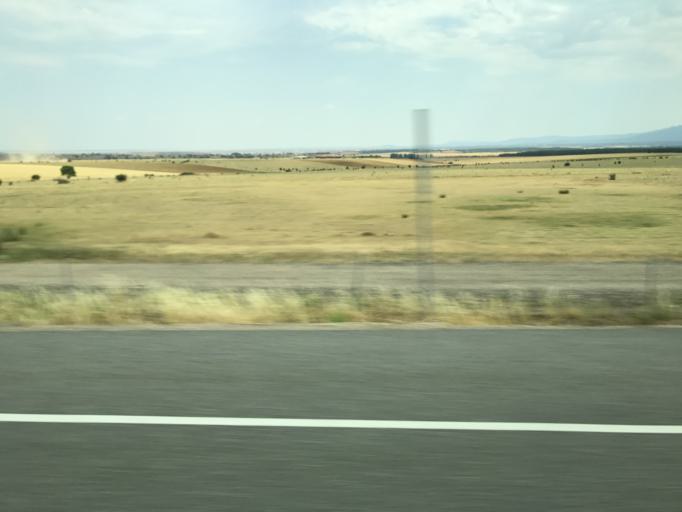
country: ES
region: Castille and Leon
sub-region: Provincia de Segovia
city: Fresno de la Fuente
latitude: 41.3849
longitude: -3.6447
